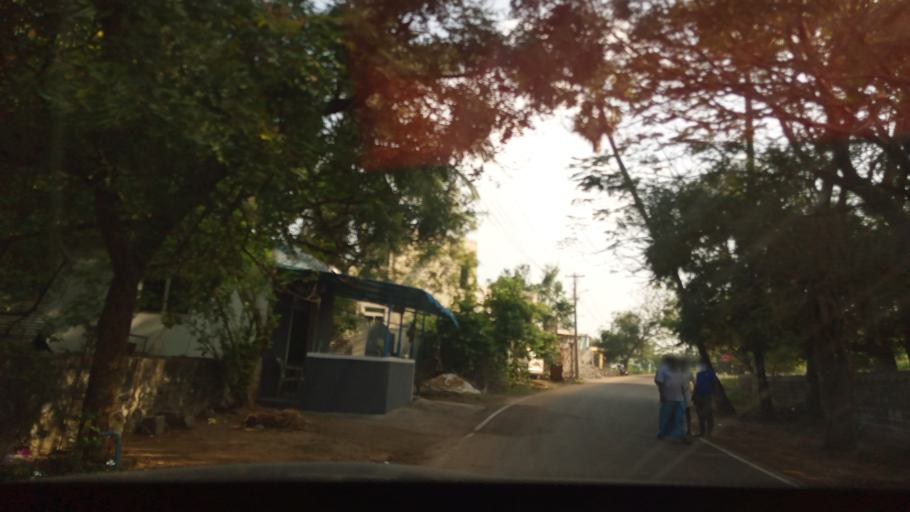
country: IN
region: Tamil Nadu
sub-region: Kancheepuram
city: Mamallapuram
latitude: 12.7629
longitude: 80.2444
